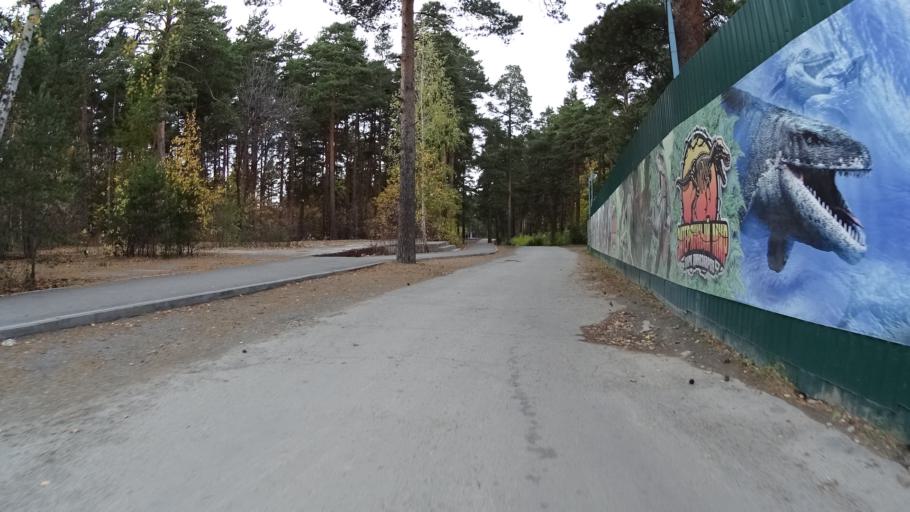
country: RU
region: Chelyabinsk
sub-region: Gorod Chelyabinsk
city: Chelyabinsk
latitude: 55.1666
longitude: 61.3656
